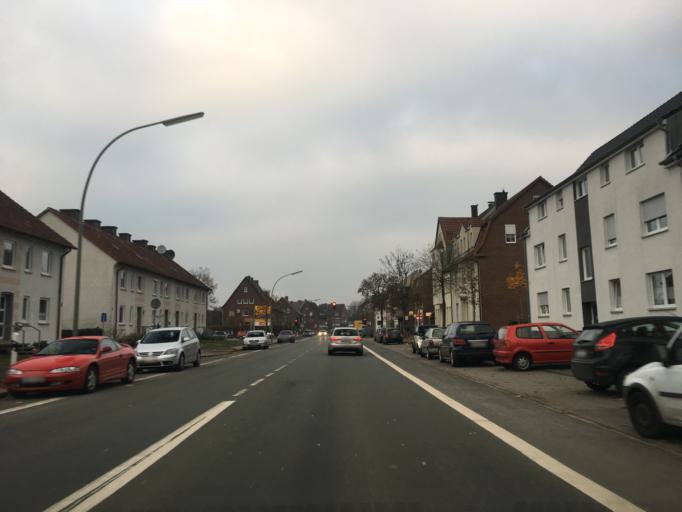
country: DE
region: North Rhine-Westphalia
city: Ludinghausen
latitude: 51.7648
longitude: 7.4359
